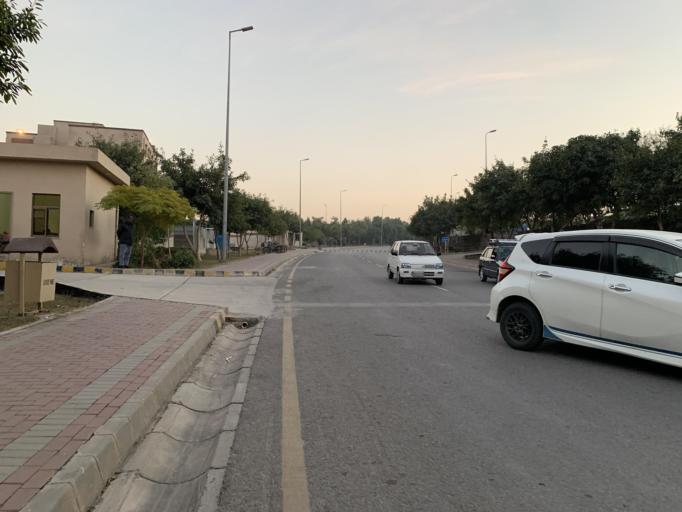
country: PK
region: Punjab
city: Rawalpindi
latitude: 33.6446
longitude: 72.9940
